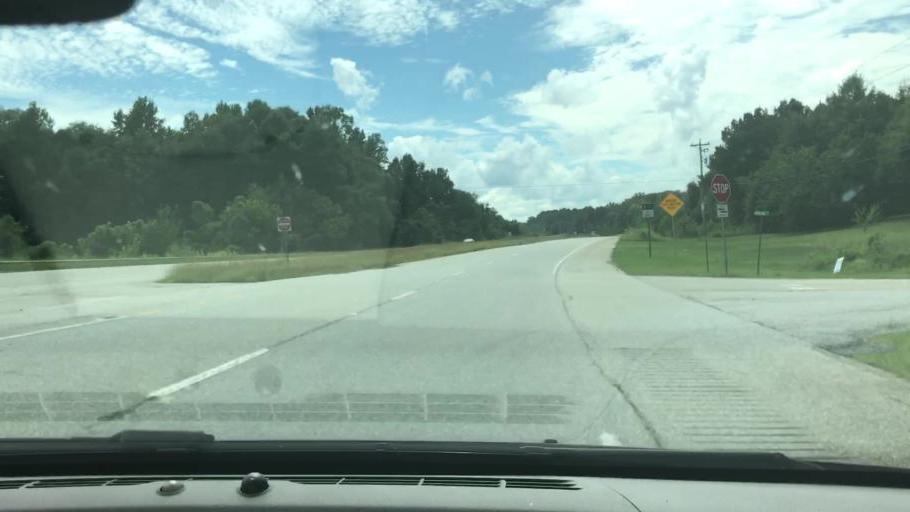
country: US
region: Georgia
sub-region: Stewart County
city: Lumpkin
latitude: 32.1568
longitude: -84.8287
